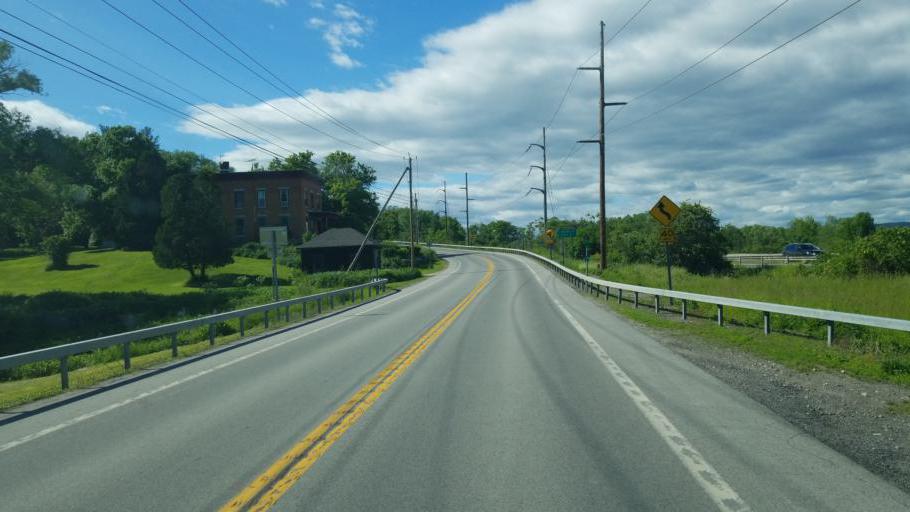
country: US
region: New York
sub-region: Montgomery County
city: Fort Plain
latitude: 42.9419
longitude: -74.6293
